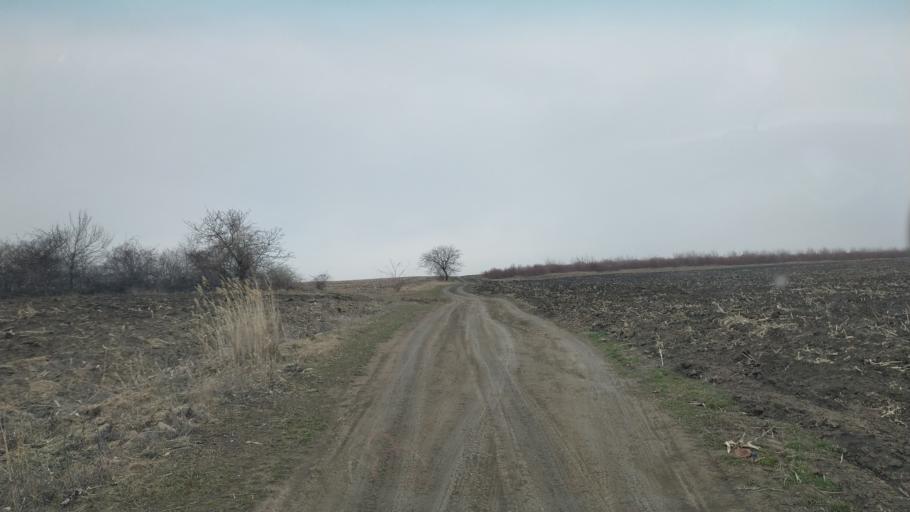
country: MD
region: Chisinau
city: Singera
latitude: 46.8278
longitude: 29.0048
